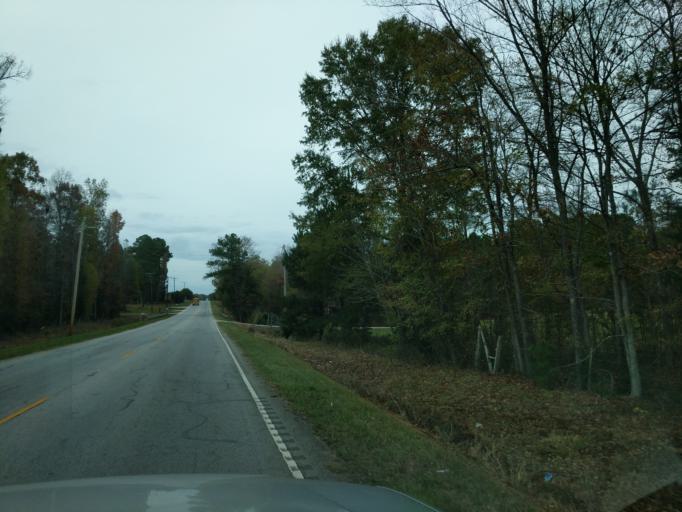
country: US
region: South Carolina
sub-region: Saluda County
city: Saluda
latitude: 34.0482
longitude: -81.7672
